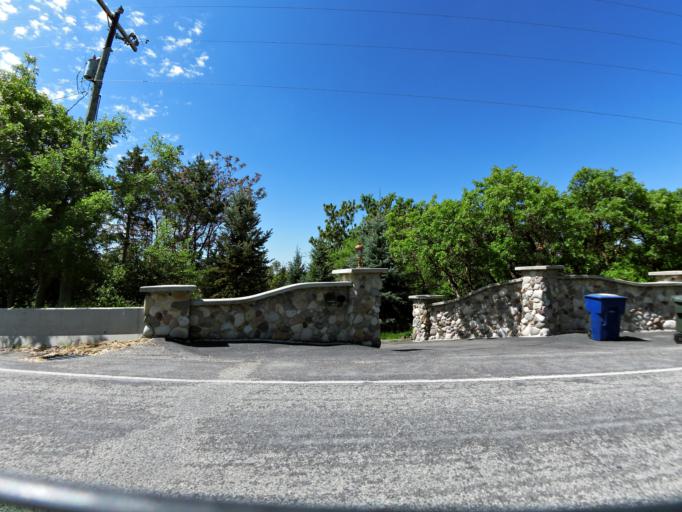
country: US
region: Utah
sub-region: Weber County
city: Washington Terrace
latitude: 41.1717
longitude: -111.9441
